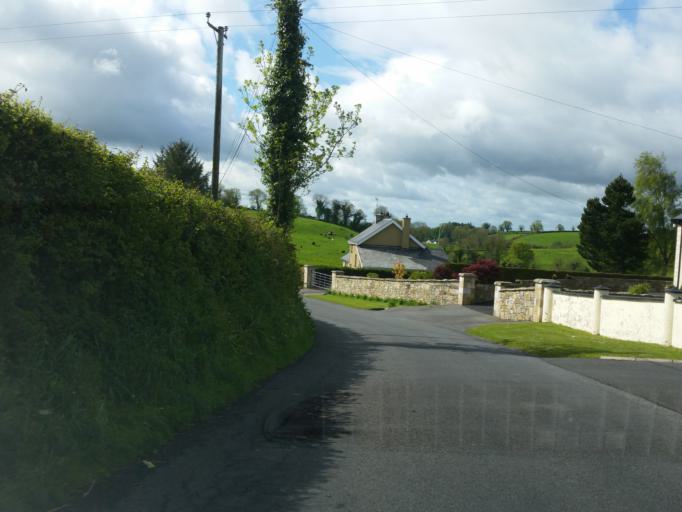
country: GB
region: Northern Ireland
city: Lisnaskea
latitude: 54.2485
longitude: -7.4218
